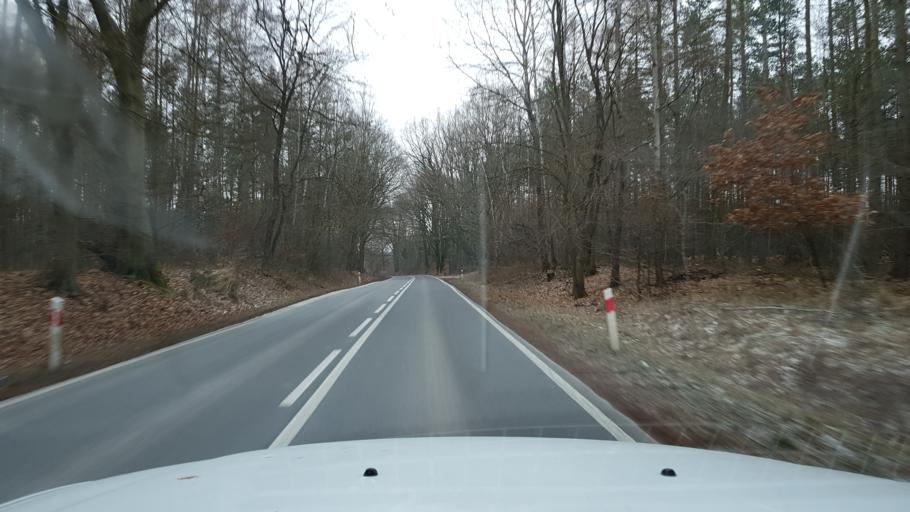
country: PL
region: West Pomeranian Voivodeship
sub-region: Powiat gryfinski
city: Gryfino
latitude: 53.1951
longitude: 14.5241
